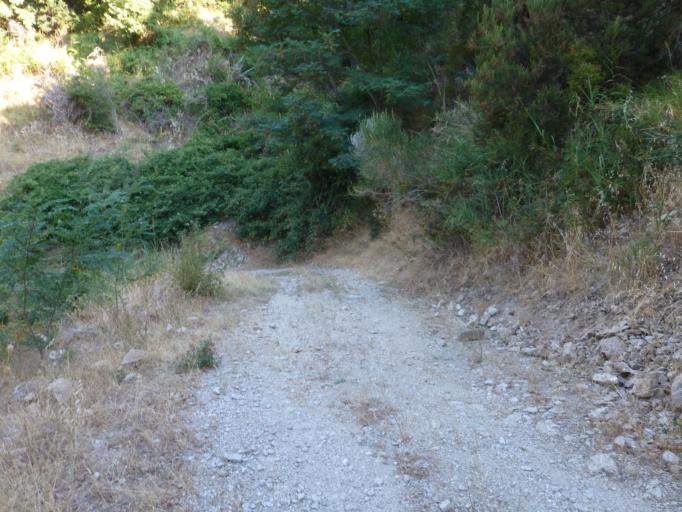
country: IT
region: Calabria
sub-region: Provincia di Reggio Calabria
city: Bivongi
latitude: 38.4999
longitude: 16.4278
